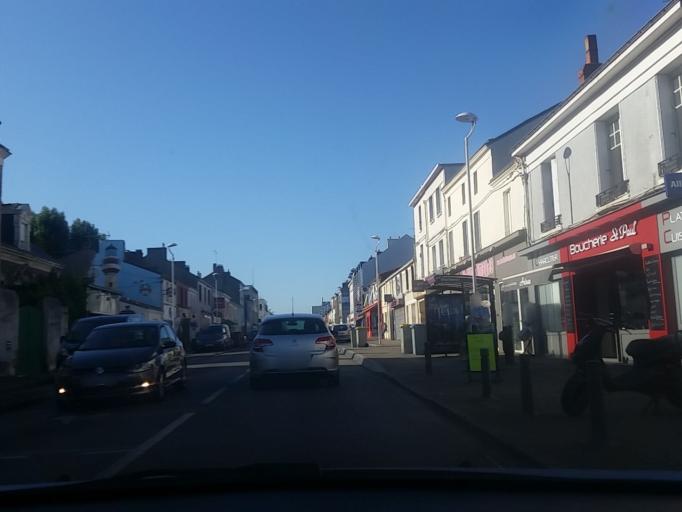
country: FR
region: Pays de la Loire
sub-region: Departement de la Loire-Atlantique
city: Reze
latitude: 47.1847
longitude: -1.5463
